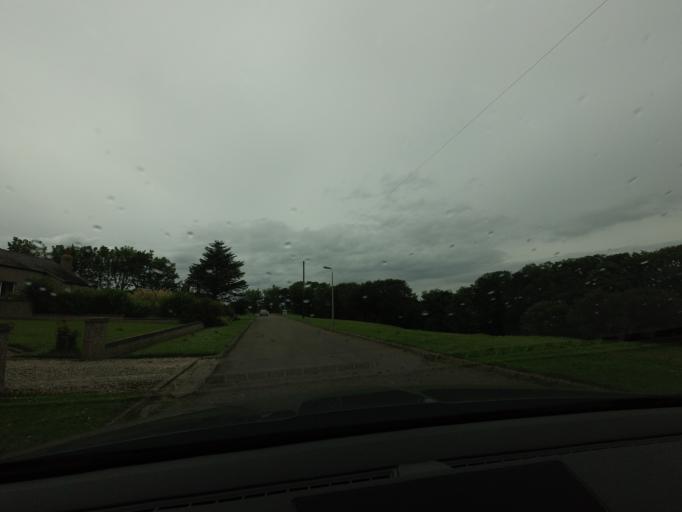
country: GB
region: Scotland
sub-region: Aberdeenshire
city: Portsoy
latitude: 57.6776
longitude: -2.7369
